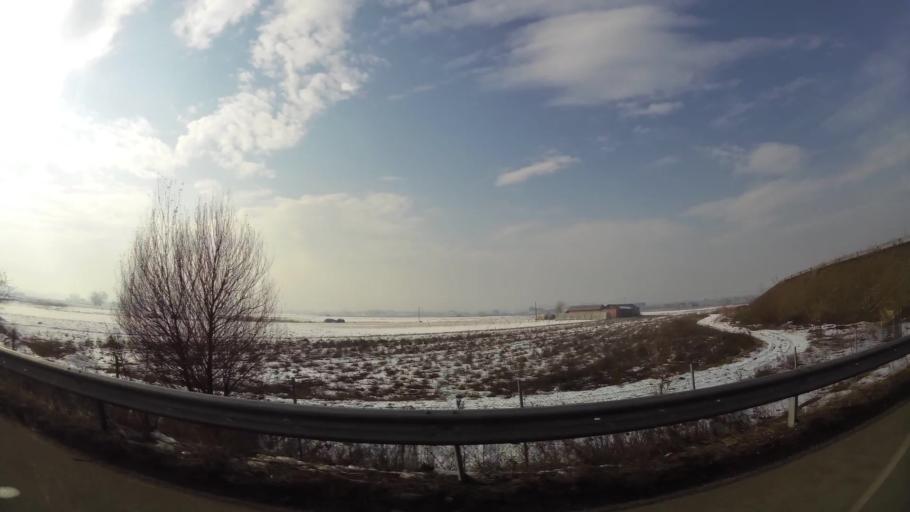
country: MK
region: Aracinovo
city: Arachinovo
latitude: 42.0068
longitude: 21.5350
